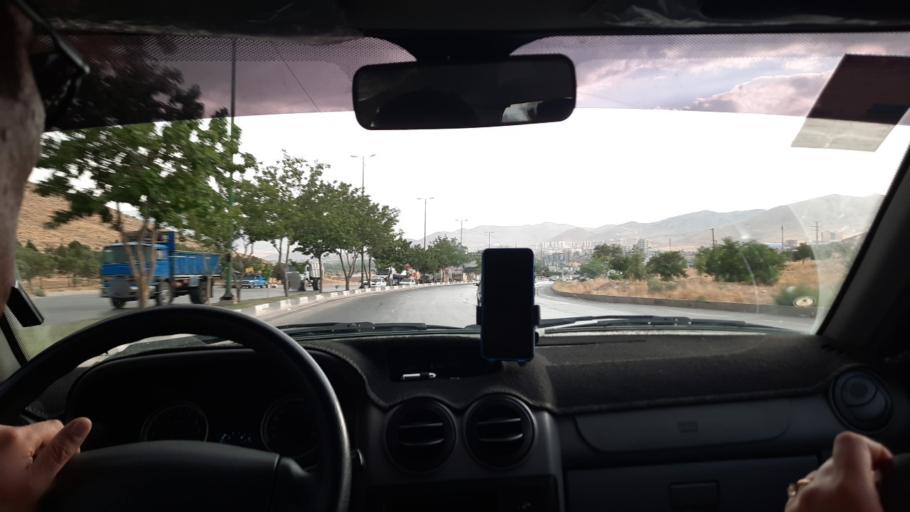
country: IR
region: Markazi
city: Arak
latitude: 34.0793
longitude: 49.6515
